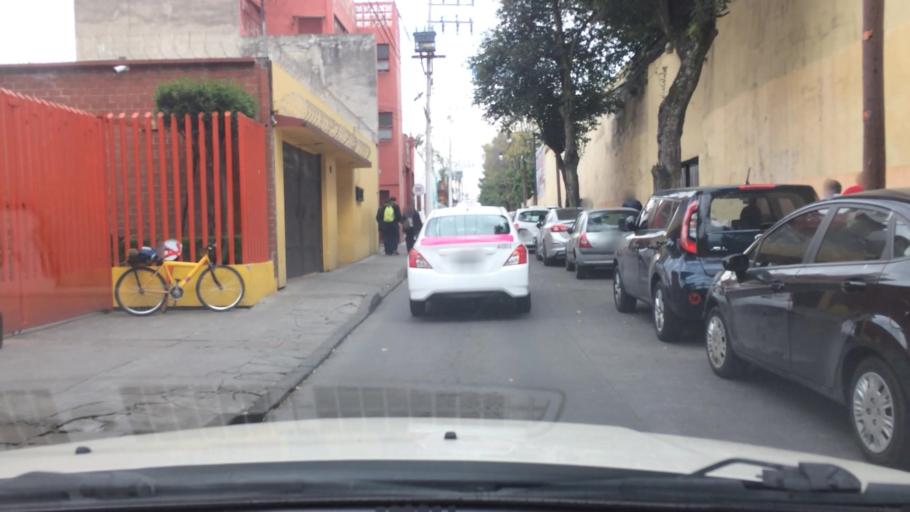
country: MX
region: Mexico City
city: Tlalpan
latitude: 19.2882
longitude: -99.1683
